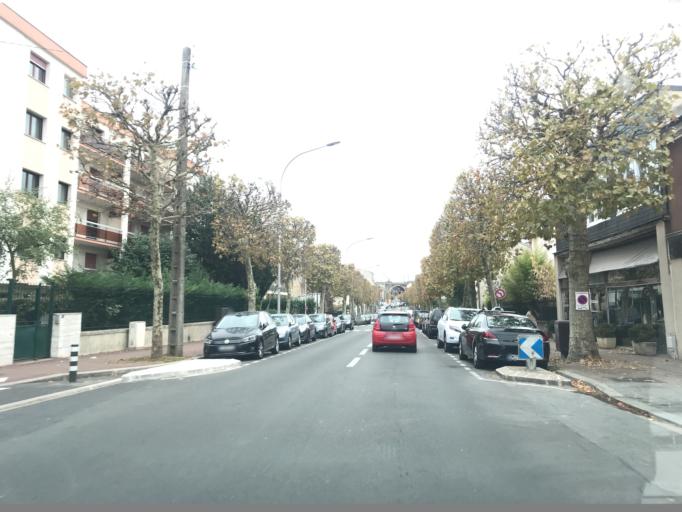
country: FR
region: Ile-de-France
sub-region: Departement du Val-de-Marne
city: Le Perreux-sur-Marne
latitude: 48.8351
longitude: 2.5017
